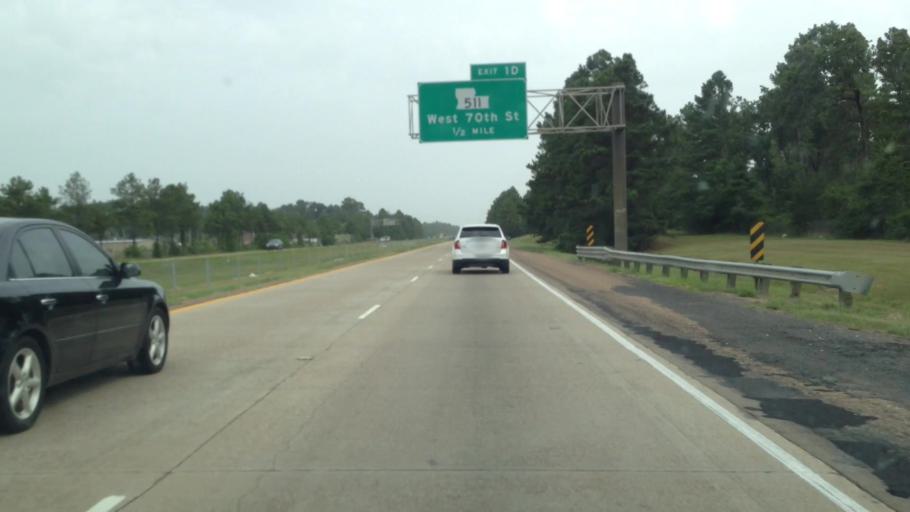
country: US
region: Louisiana
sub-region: Caddo Parish
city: Shreveport
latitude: 32.4317
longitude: -93.8398
